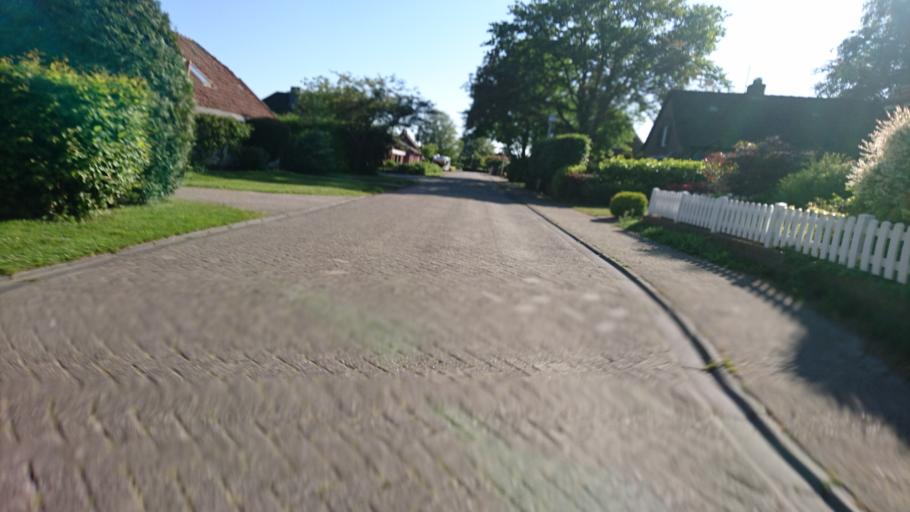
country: DE
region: Lower Saxony
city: Norden
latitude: 53.5863
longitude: 7.2156
